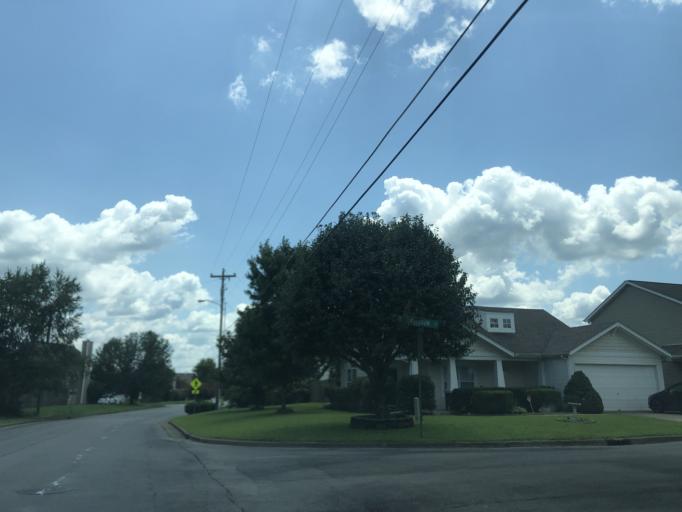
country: US
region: Tennessee
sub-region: Wilson County
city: Green Hill
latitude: 36.2205
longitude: -86.5942
